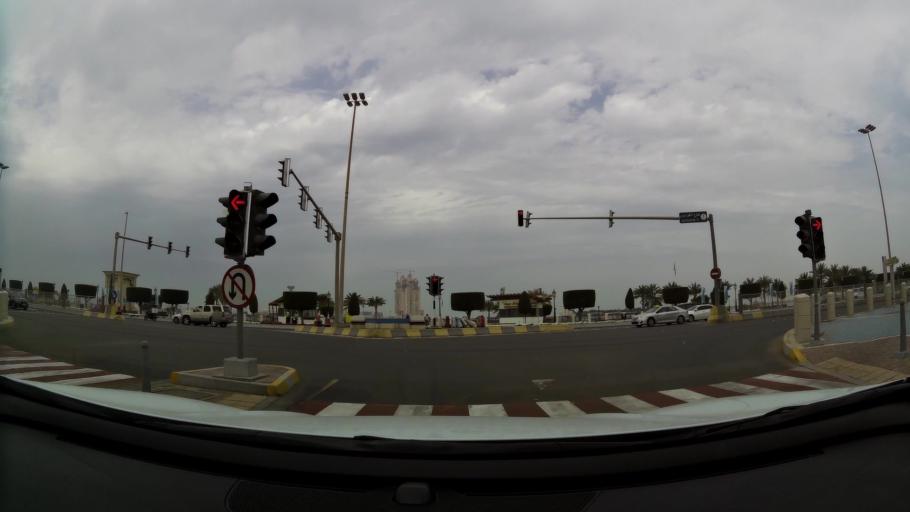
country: AE
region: Abu Dhabi
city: Abu Dhabi
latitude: 24.4679
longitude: 54.3329
